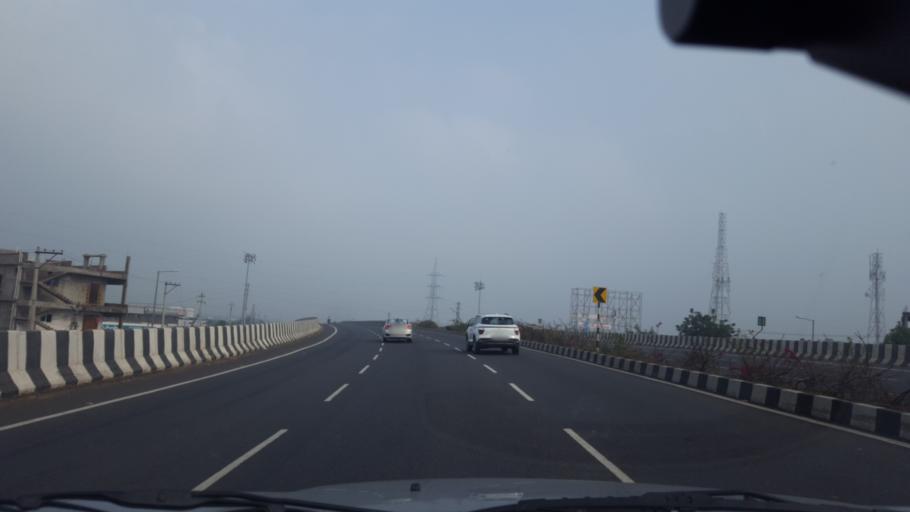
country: IN
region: Andhra Pradesh
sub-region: Prakasam
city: Ongole
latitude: 15.5513
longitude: 80.0561
